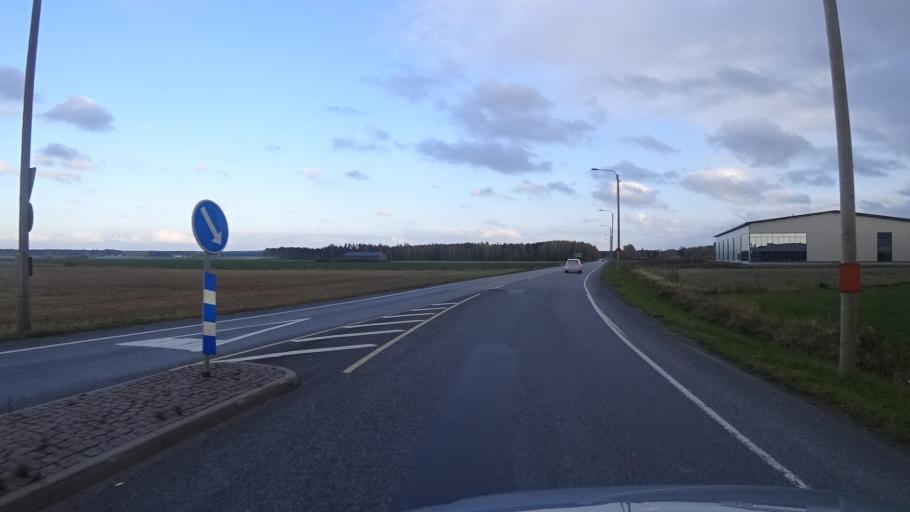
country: FI
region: Satakunta
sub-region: Rauma
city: Saekylae
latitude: 61.0463
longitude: 22.3599
